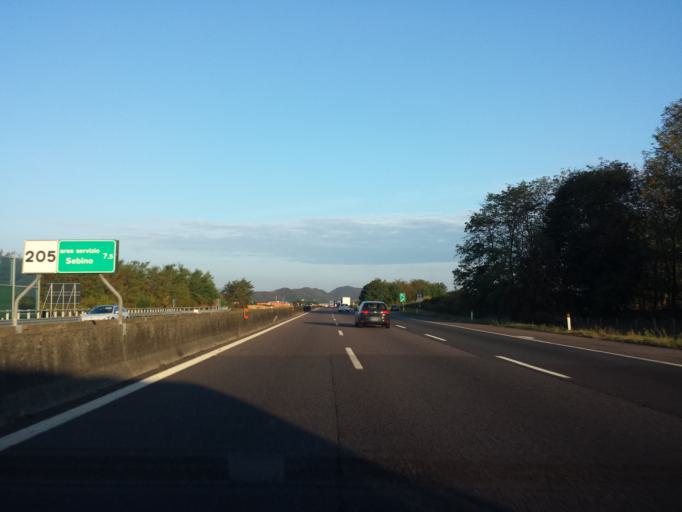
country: IT
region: Lombardy
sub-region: Provincia di Brescia
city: Costa-Barco
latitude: 45.5687
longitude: 10.0522
